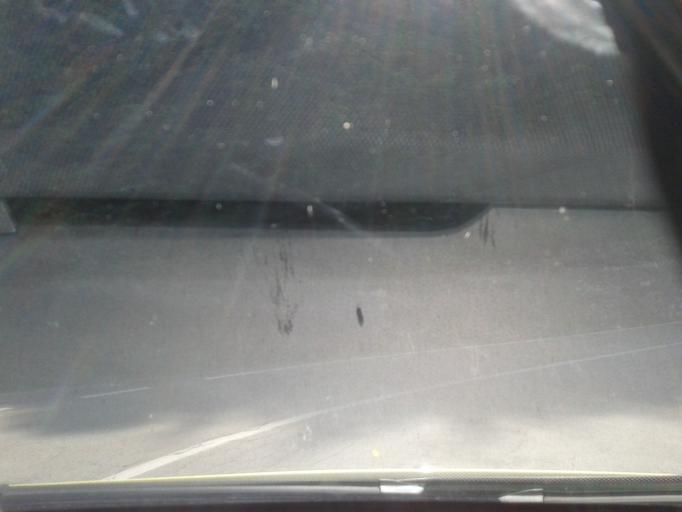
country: RO
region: Sibiu
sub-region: Comuna Cartisoara
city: Cartisoara
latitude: 45.6645
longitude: 24.5949
